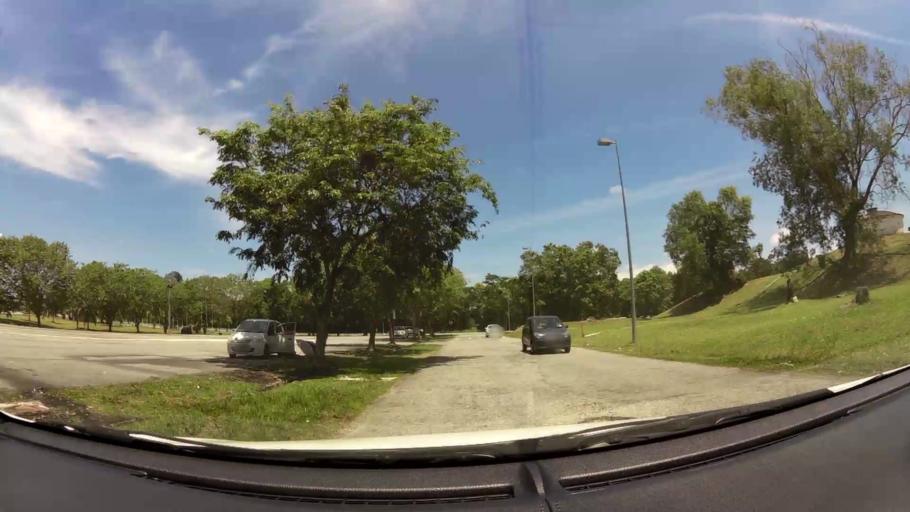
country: BN
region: Brunei and Muara
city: Bandar Seri Begawan
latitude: 4.9310
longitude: 114.9453
